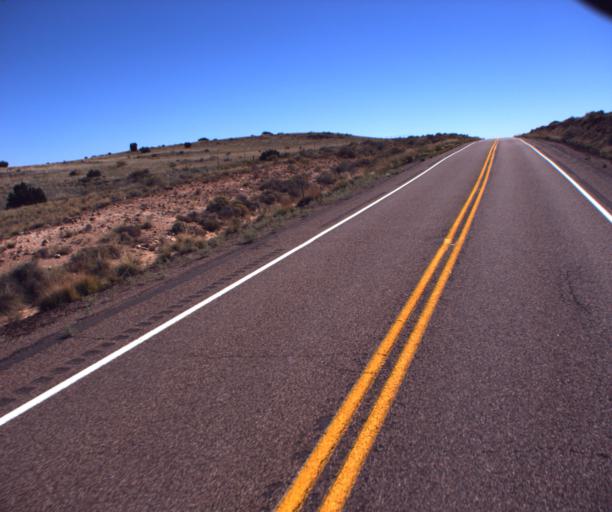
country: US
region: Arizona
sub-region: Apache County
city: Saint Johns
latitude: 34.5614
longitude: -109.5031
